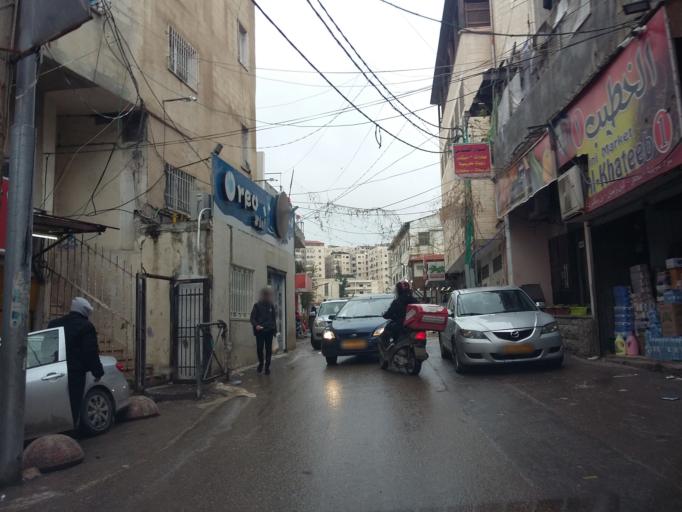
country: PS
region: West Bank
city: `Anata
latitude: 31.8115
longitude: 35.2460
